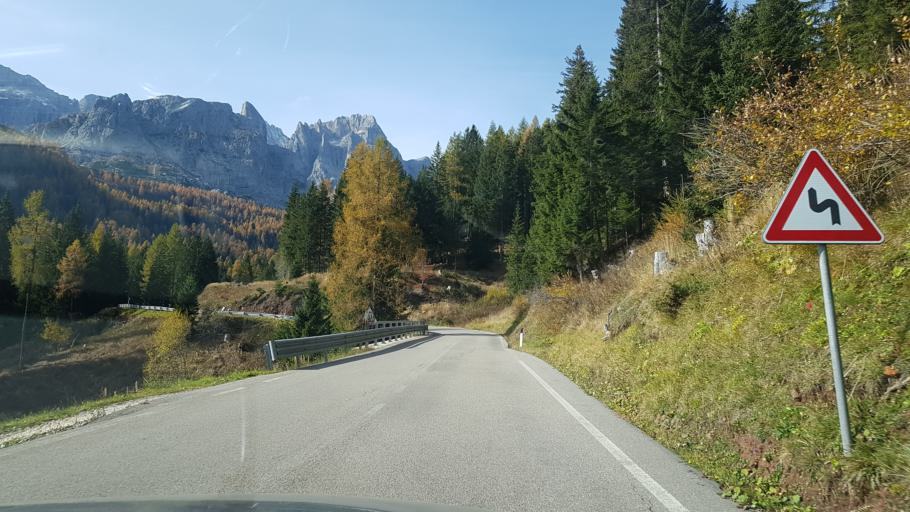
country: IT
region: Veneto
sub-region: Provincia di Belluno
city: Auronzo
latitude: 46.6520
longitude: 12.4356
